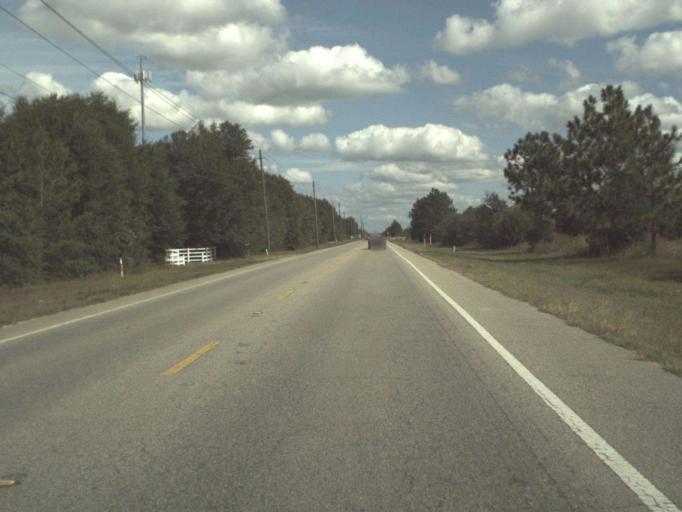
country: US
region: Florida
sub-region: Okaloosa County
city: Crestview
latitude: 30.7503
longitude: -86.4660
